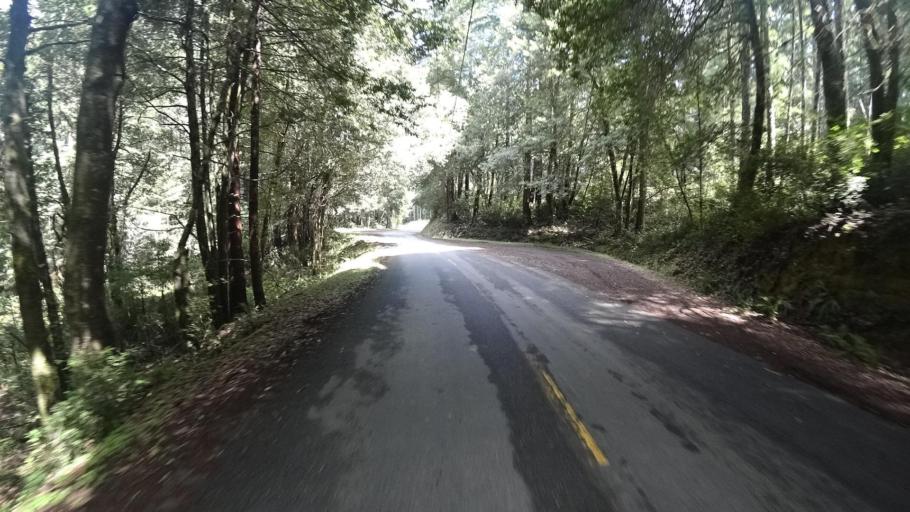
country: US
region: California
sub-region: Humboldt County
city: Blue Lake
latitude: 40.7588
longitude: -123.9680
